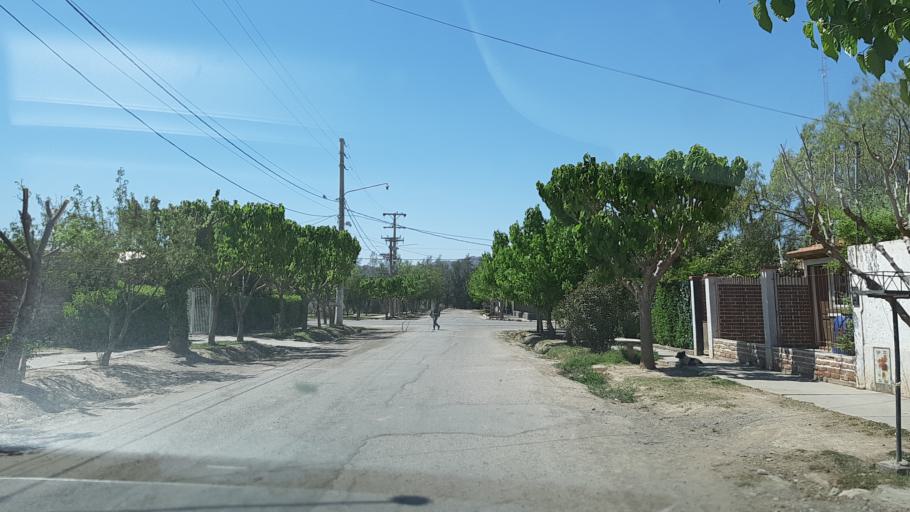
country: AR
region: San Juan
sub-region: Departamento de Zonda
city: Zonda
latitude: -31.5381
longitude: -68.7520
